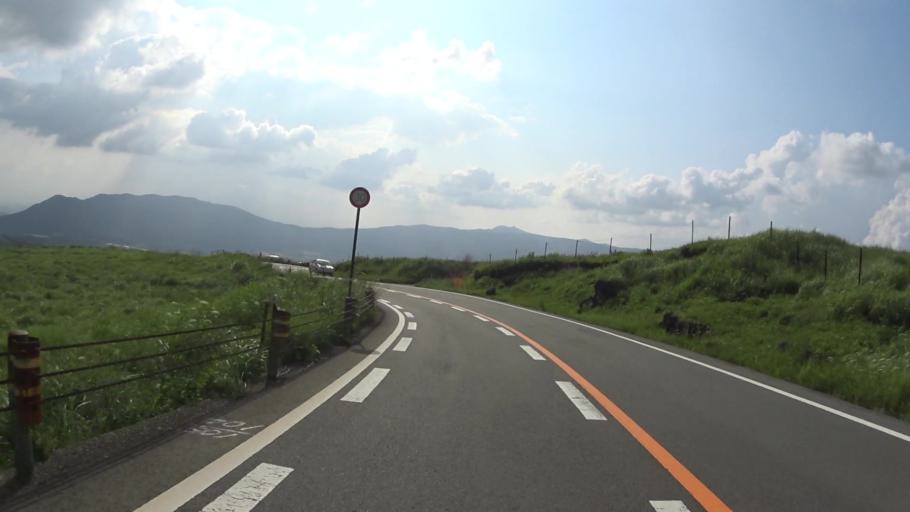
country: JP
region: Kumamoto
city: Aso
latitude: 32.9031
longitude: 131.0391
